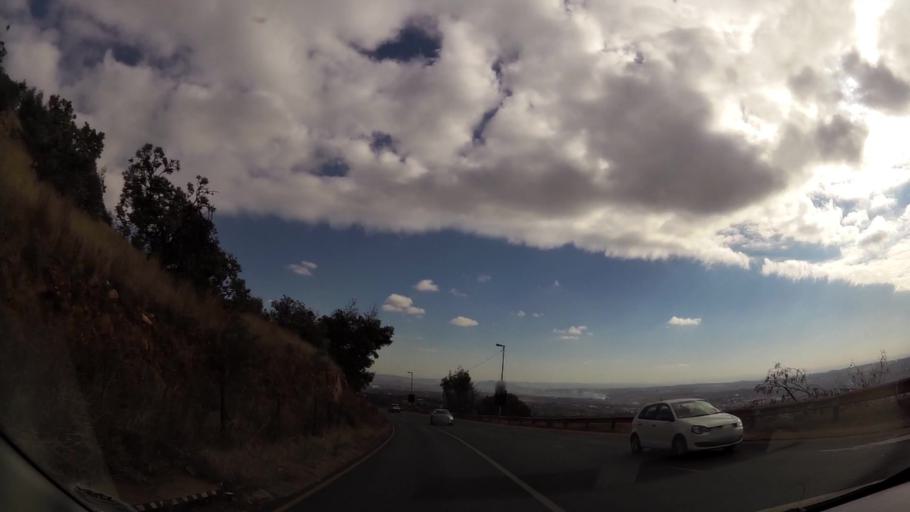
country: ZA
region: Gauteng
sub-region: City of Johannesburg Metropolitan Municipality
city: Roodepoort
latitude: -26.1051
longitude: 27.8666
